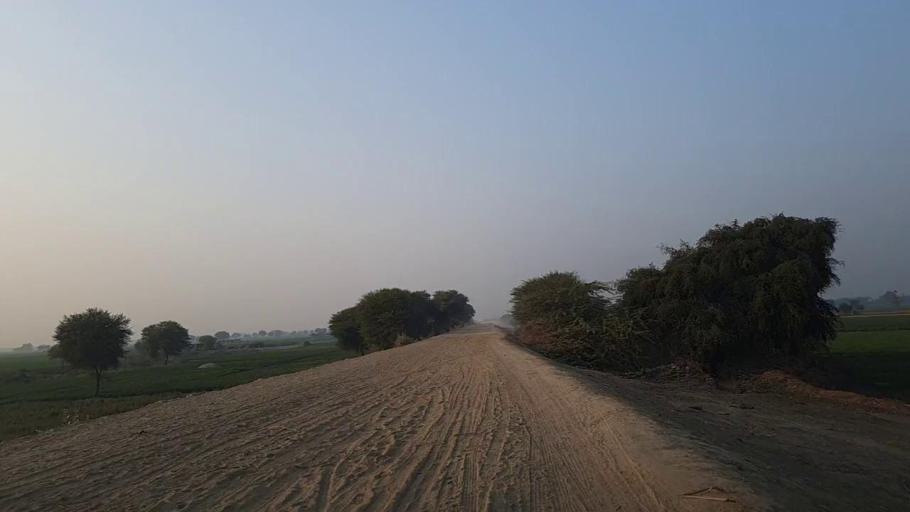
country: PK
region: Sindh
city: Sann
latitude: 26.1803
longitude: 68.0954
